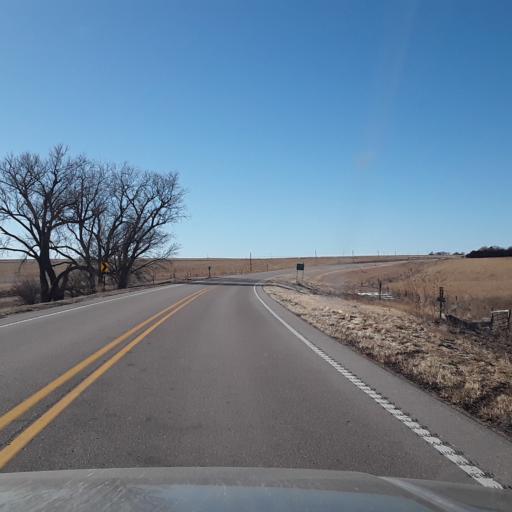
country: US
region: Nebraska
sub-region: Frontier County
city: Stockville
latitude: 40.7010
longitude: -100.2551
